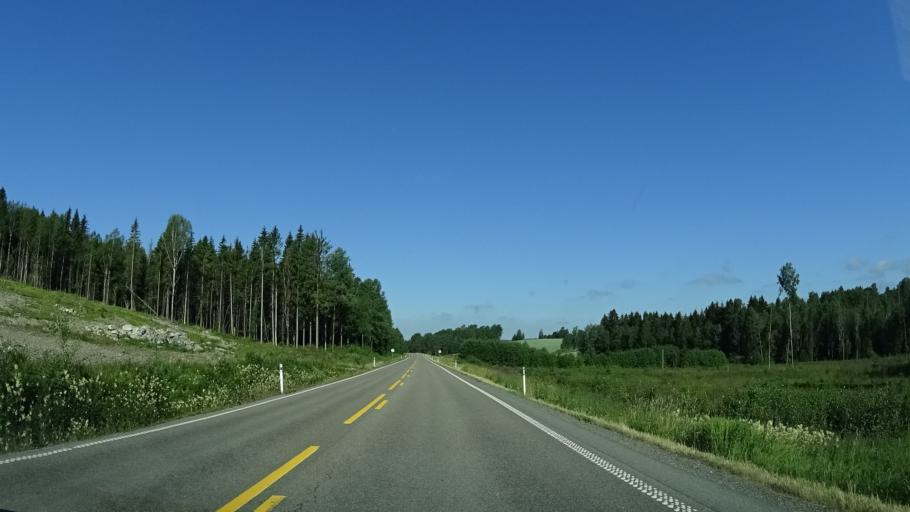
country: NO
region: Akershus
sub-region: Ski
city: Ski
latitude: 59.6814
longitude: 10.8537
